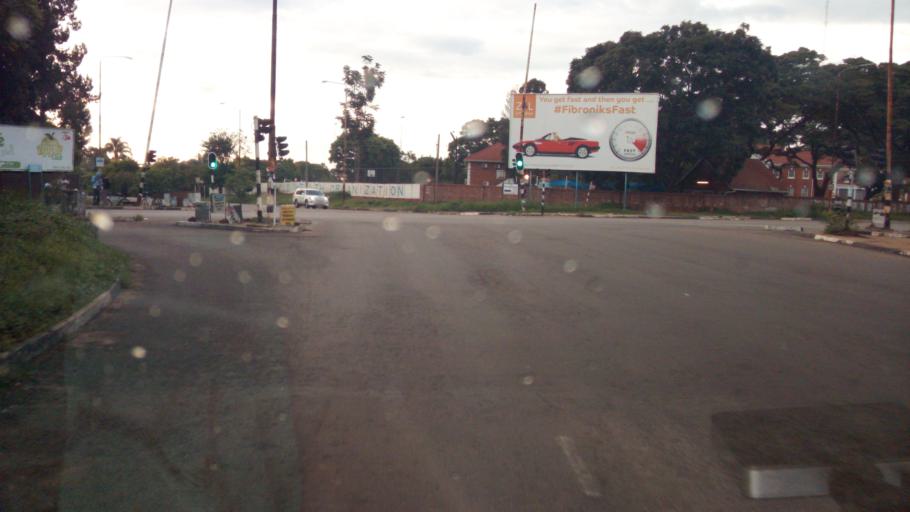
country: ZW
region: Harare
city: Harare
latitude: -17.8008
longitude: 31.0881
